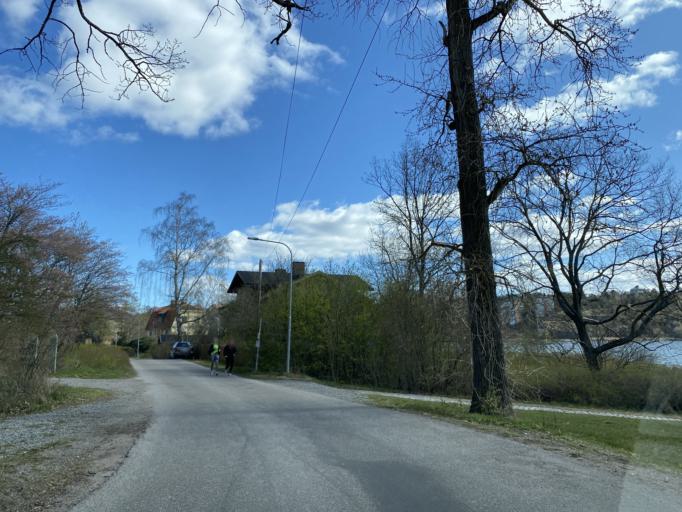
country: SE
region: Stockholm
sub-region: Nacka Kommun
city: Nacka
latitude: 59.3215
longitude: 18.1486
